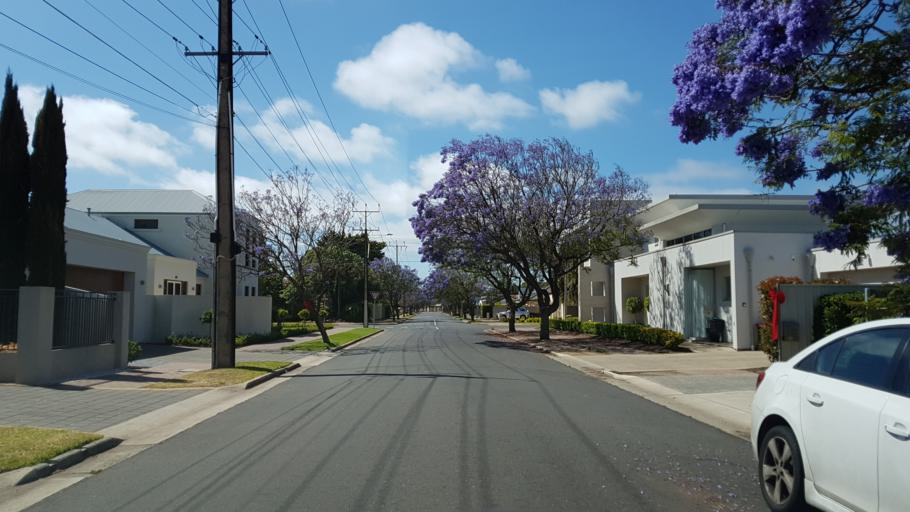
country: AU
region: South Australia
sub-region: Adelaide
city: Glenelg
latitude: -34.9661
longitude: 138.5177
